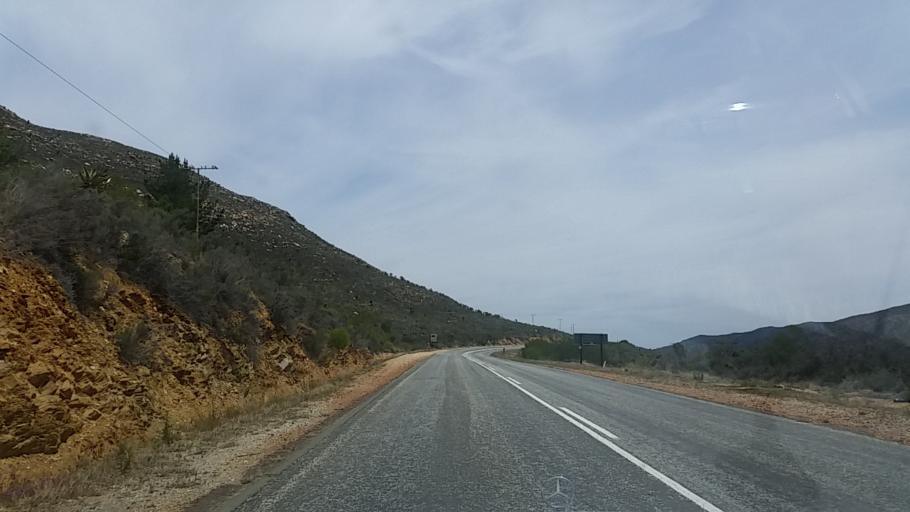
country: ZA
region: Western Cape
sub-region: Eden District Municipality
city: Knysna
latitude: -33.7462
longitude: 22.9863
